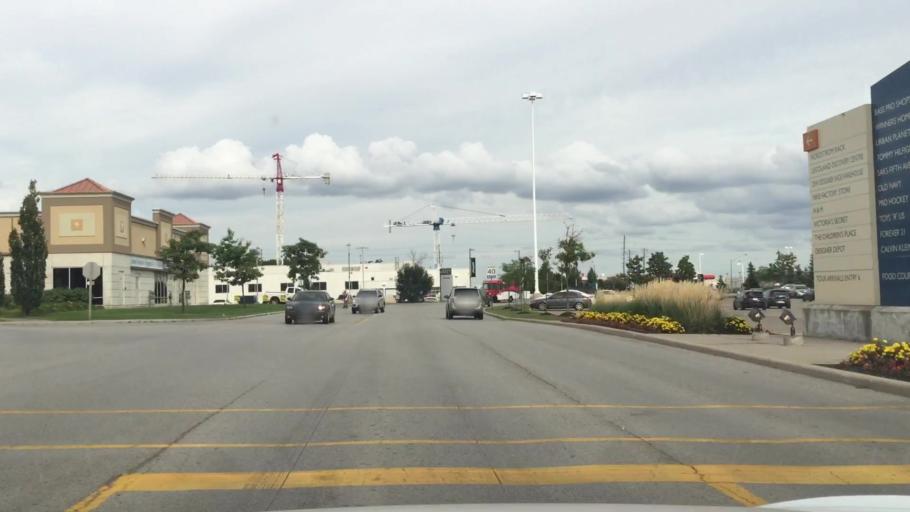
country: CA
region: Ontario
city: Vaughan
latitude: 43.8280
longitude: -79.5354
